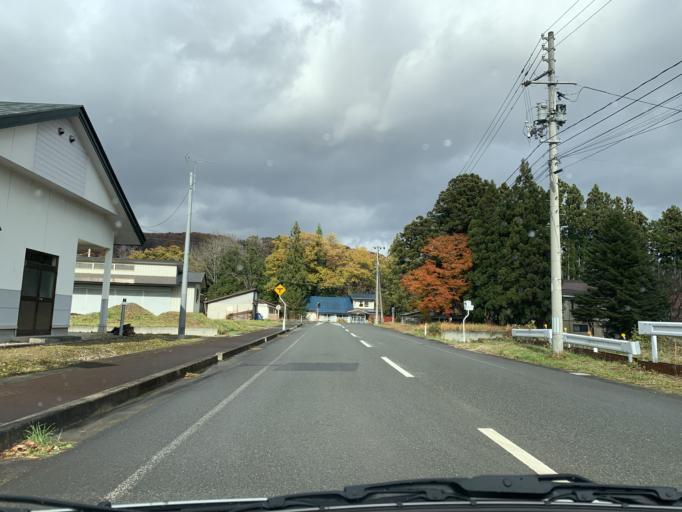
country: JP
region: Iwate
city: Mizusawa
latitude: 39.1158
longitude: 140.9459
